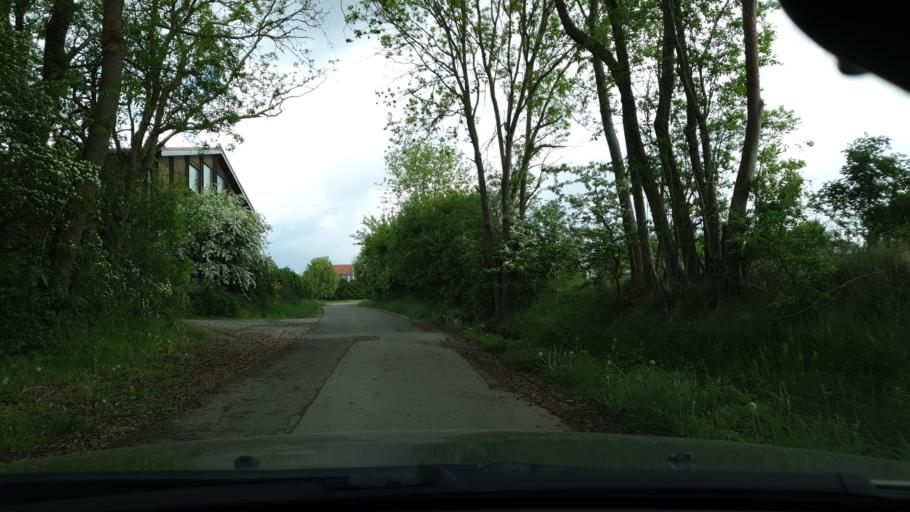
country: DE
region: Rheinland-Pfalz
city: Kaiserslautern
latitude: 49.4587
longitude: 7.7936
